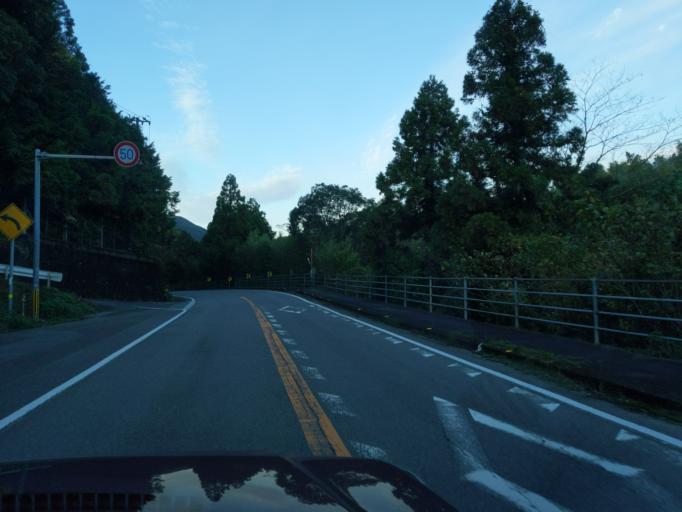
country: JP
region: Tokushima
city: Anan
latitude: 33.6916
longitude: 134.4335
